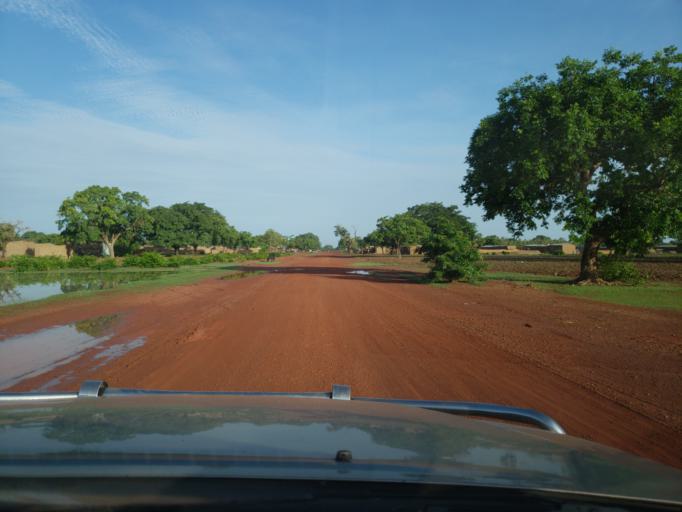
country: ML
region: Sikasso
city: Koutiala
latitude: 12.4180
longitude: -5.5752
